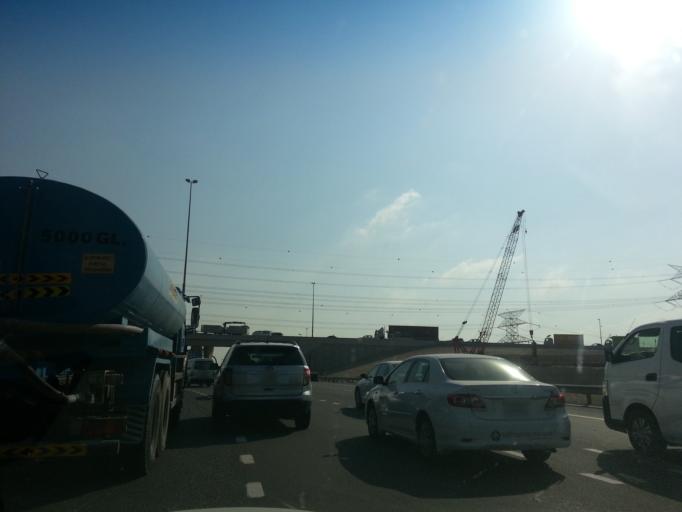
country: AE
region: Dubai
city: Dubai
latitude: 25.0172
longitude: 55.1575
